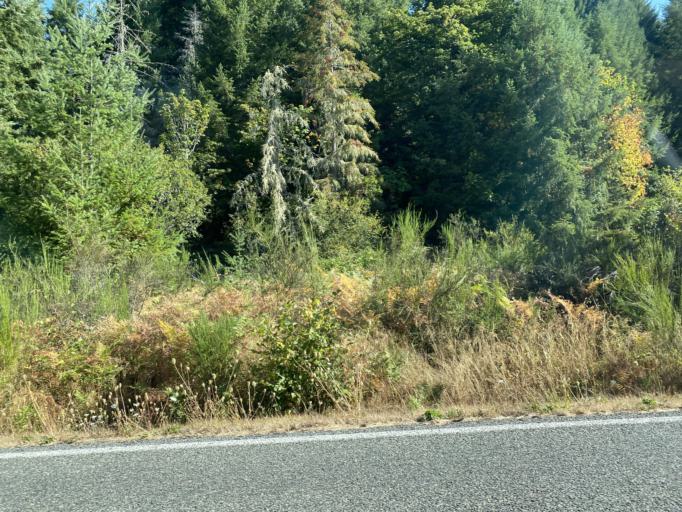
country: US
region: Washington
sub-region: Thurston County
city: Rainier
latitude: 46.9023
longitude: -122.7616
